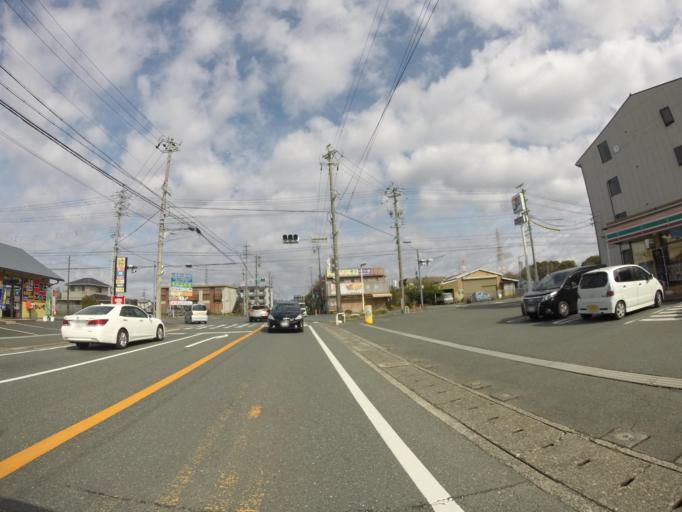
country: JP
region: Shizuoka
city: Hamakita
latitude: 34.7997
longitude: 137.6984
